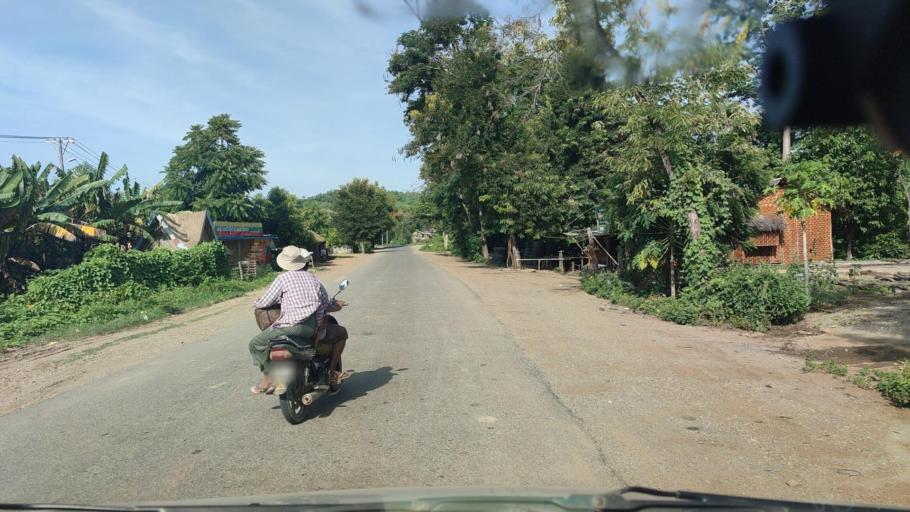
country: MM
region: Magway
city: Minbu
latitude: 20.0453
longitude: 94.6010
